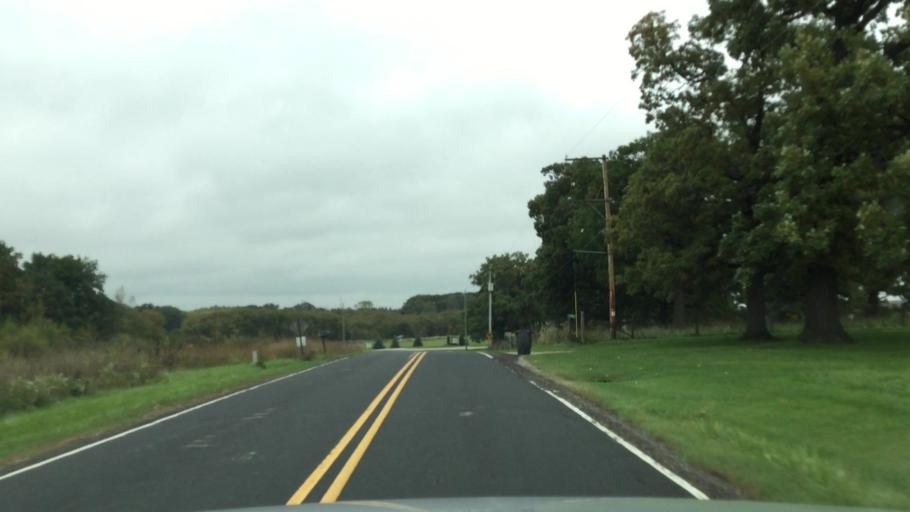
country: US
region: Wisconsin
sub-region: Racine County
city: Waterford
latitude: 42.7614
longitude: -88.1656
